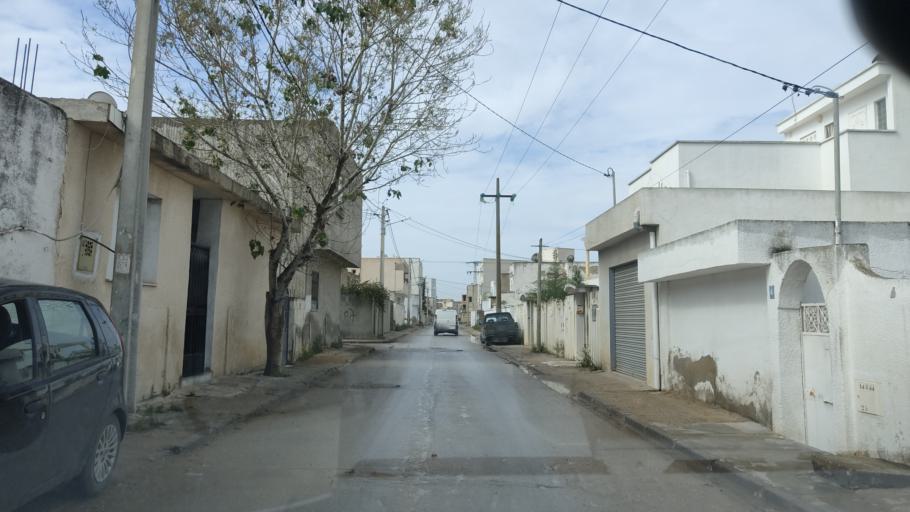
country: TN
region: Ariana
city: Ariana
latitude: 36.8881
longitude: 10.2147
